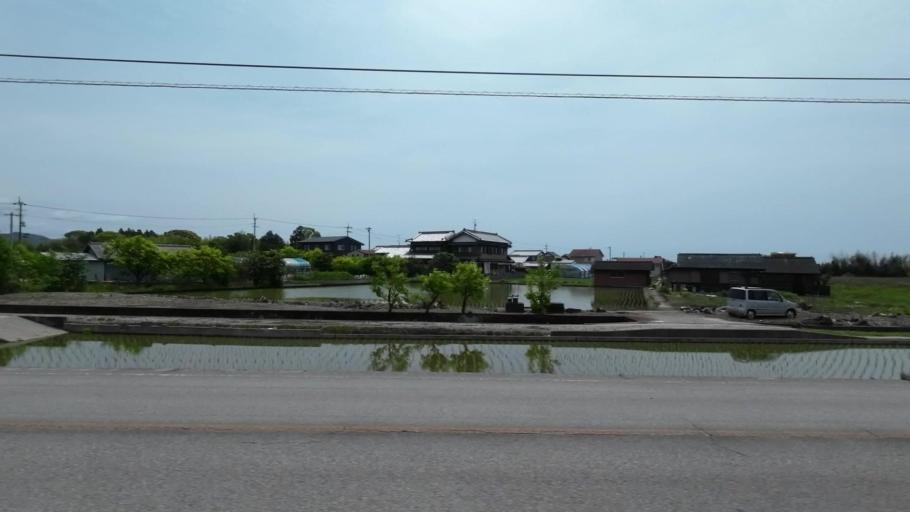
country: JP
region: Kochi
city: Kochi-shi
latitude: 33.5868
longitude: 133.6565
